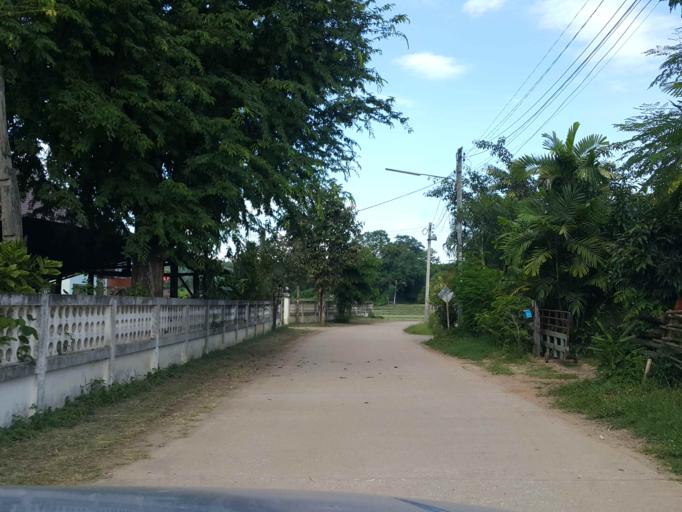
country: TH
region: Chiang Mai
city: Mae Taeng
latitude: 18.9719
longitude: 98.9159
